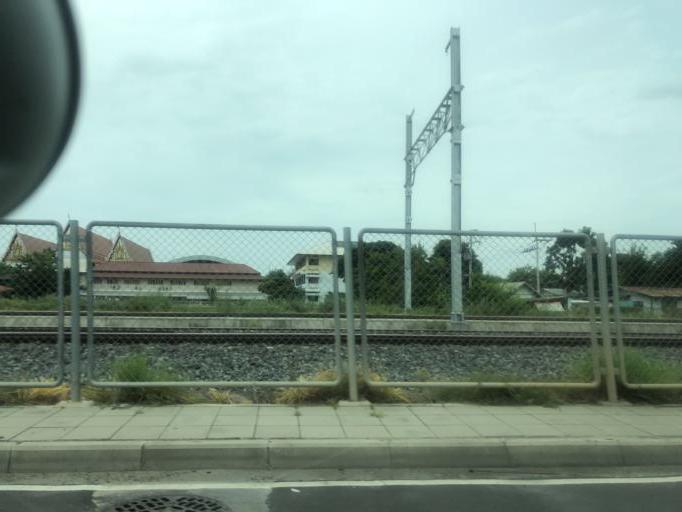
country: TH
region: Bangkok
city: Don Mueang
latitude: 13.9625
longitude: 100.6055
